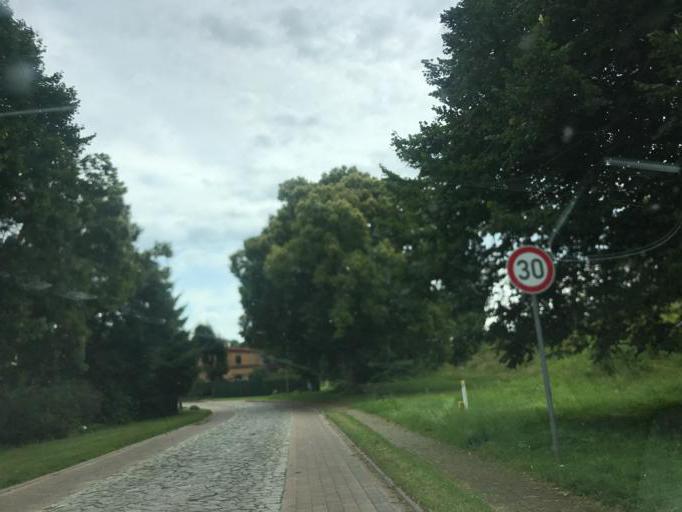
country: DE
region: Mecklenburg-Vorpommern
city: Mollenhagen
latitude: 53.4288
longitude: 12.9386
